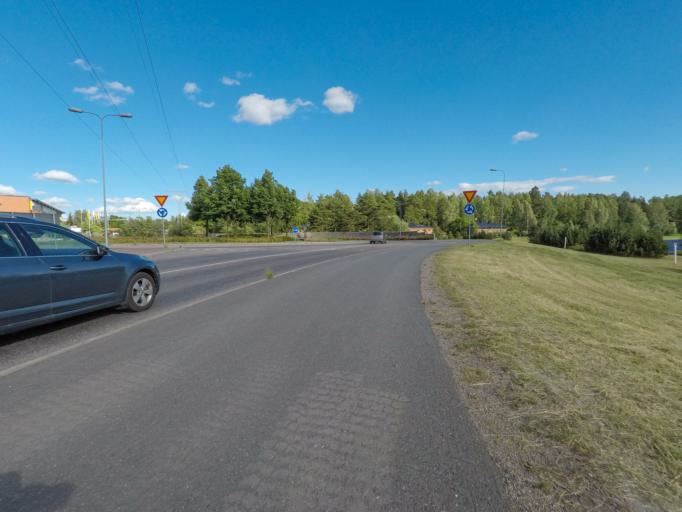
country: FI
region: South Karelia
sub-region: Lappeenranta
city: Lappeenranta
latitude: 61.0644
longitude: 28.1690
